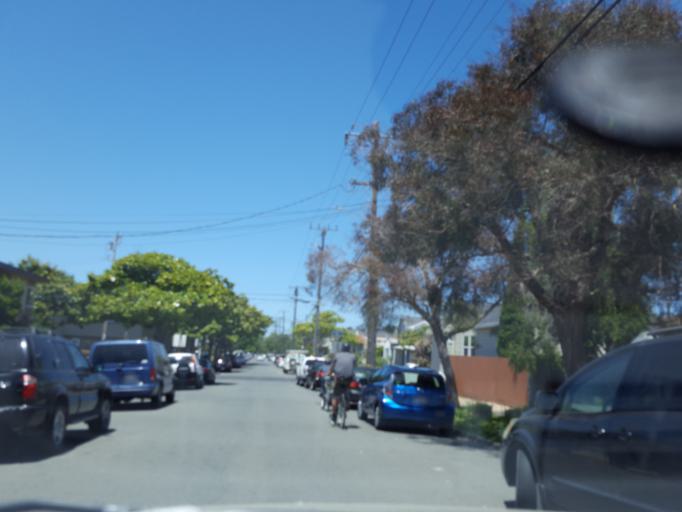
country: US
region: California
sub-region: Contra Costa County
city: El Cerrito
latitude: 37.9179
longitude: -122.3100
